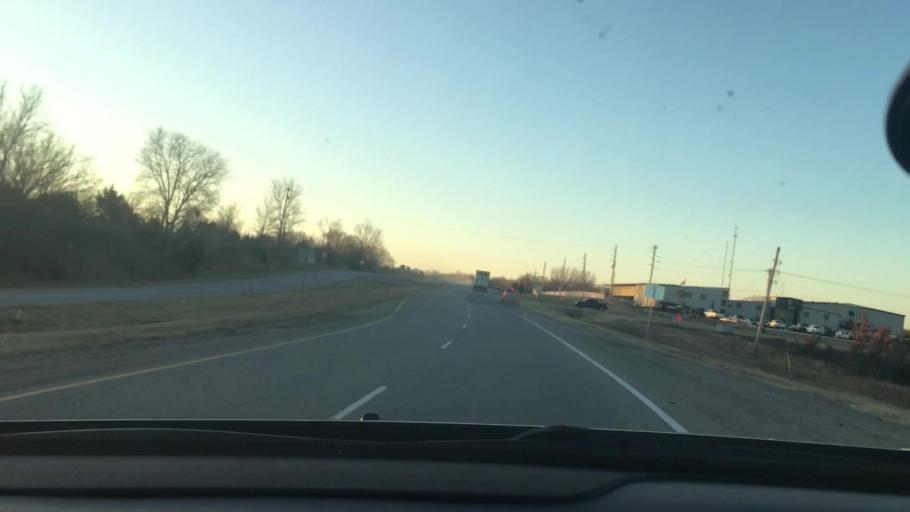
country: US
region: Oklahoma
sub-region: Pontotoc County
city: Ada
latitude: 34.7397
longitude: -96.7093
